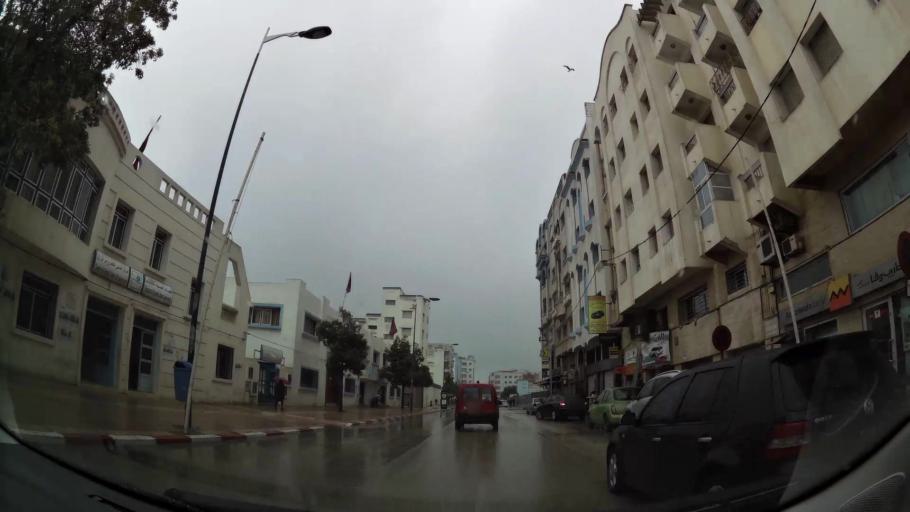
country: MA
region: Taza-Al Hoceima-Taounate
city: Al Hoceima
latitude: 35.2485
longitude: -3.9342
